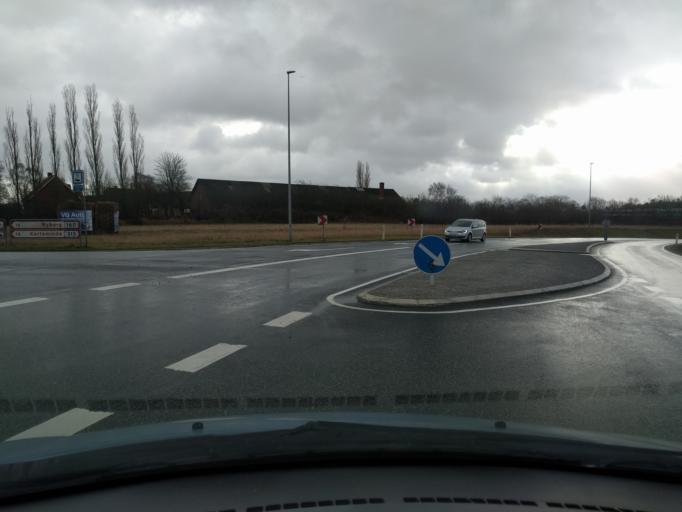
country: DK
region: South Denmark
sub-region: Kerteminde Kommune
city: Langeskov
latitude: 55.3661
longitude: 10.5747
